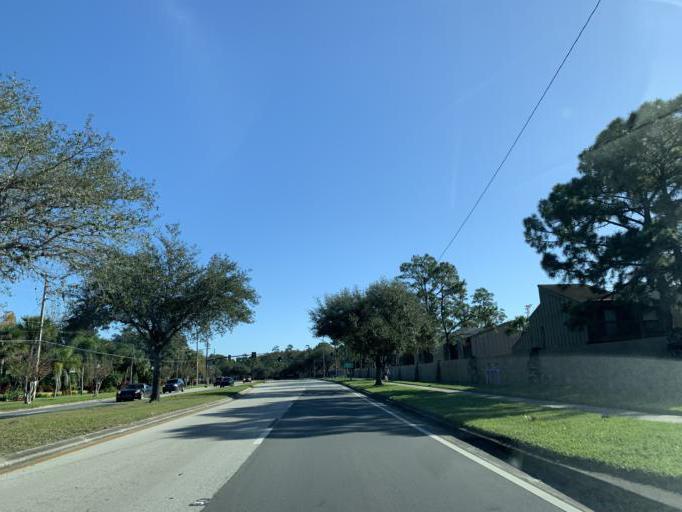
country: US
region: Florida
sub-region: Orange County
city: Oak Ridge
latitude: 28.4941
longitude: -81.4542
